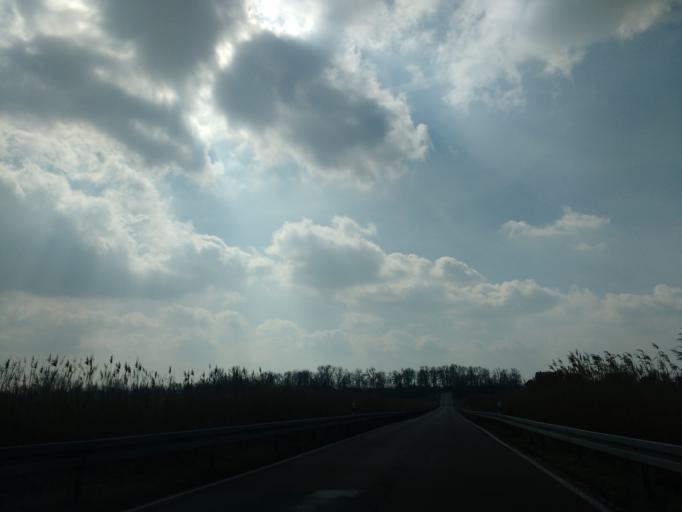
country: DE
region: Saxony-Anhalt
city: Roblingen am See
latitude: 51.4734
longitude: 11.6763
